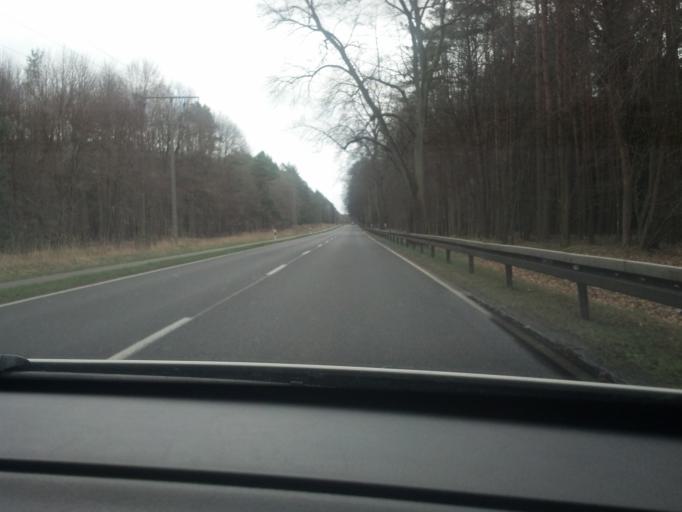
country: DE
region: Mecklenburg-Vorpommern
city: Wesenberg
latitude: 53.2716
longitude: 12.8594
